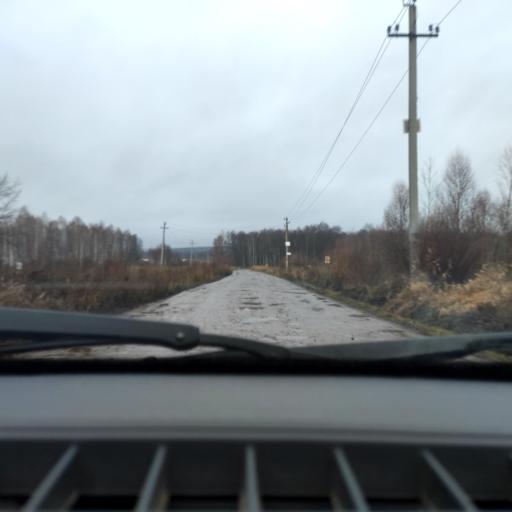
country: RU
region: Bashkortostan
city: Avdon
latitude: 54.6318
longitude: 55.7329
